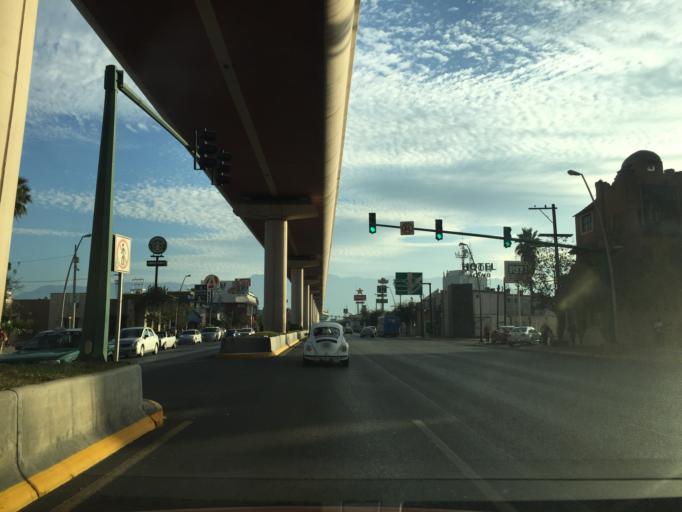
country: MX
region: Nuevo Leon
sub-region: San Nicolas de los Garza
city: San Nicolas de los Garza
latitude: 25.7389
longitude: -100.3030
